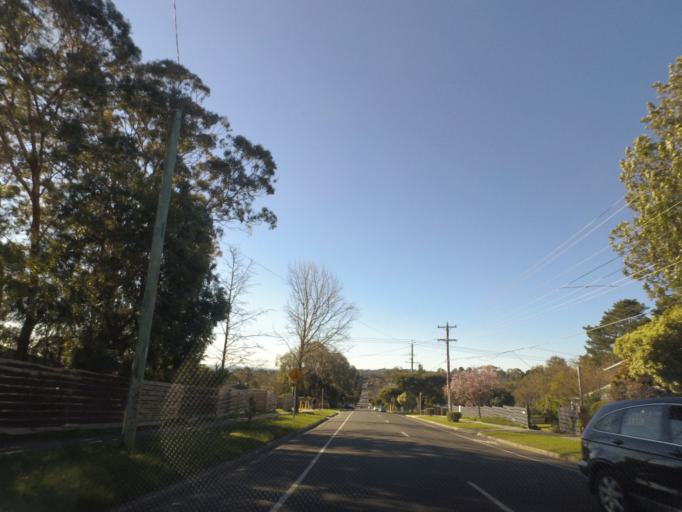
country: AU
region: Victoria
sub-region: Yarra Ranges
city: Kilsyth
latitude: -37.7982
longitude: 145.3131
